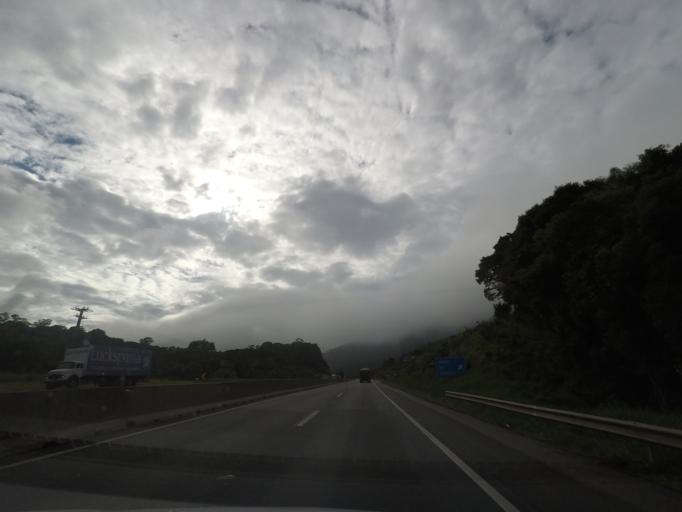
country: BR
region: Parana
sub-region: Campina Grande Do Sul
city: Campina Grande do Sul
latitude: -25.1766
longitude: -48.8761
